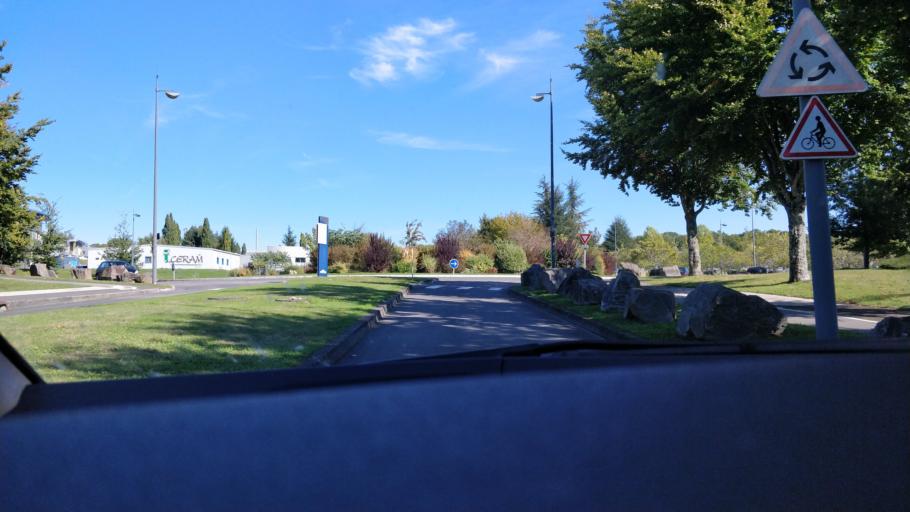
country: FR
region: Limousin
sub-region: Departement de la Haute-Vienne
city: Le Palais-sur-Vienne
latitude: 45.8604
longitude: 1.2902
